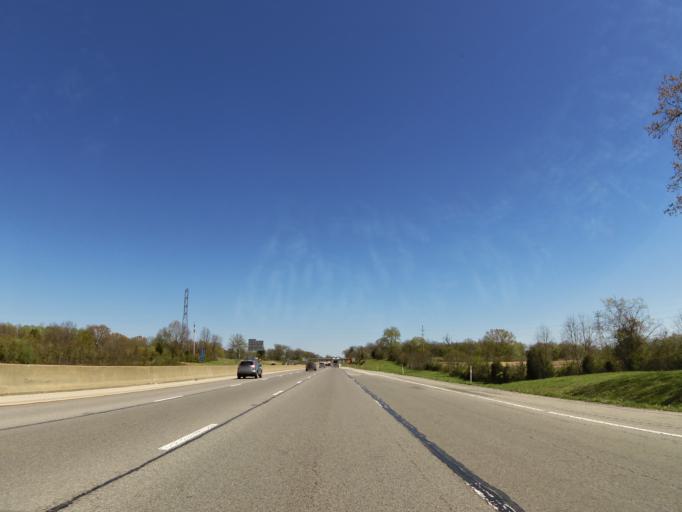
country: US
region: Kentucky
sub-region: Warren County
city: Bowling Green
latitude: 37.0082
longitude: -86.3601
